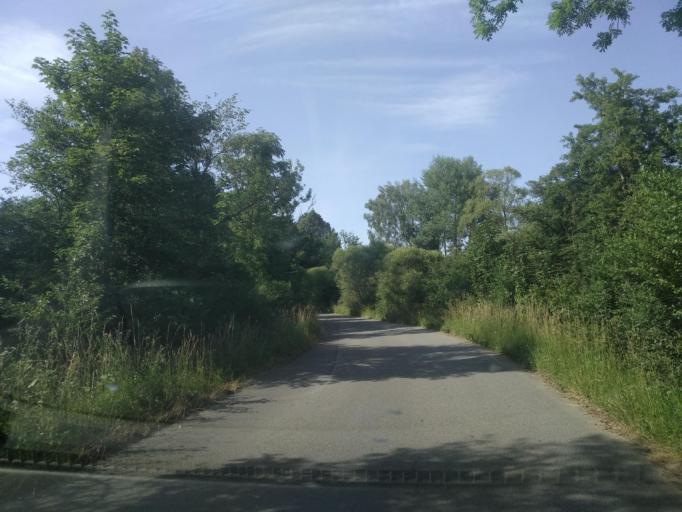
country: PL
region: Subcarpathian Voivodeship
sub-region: Powiat krosnienski
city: Jasliska
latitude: 49.4237
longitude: 21.8548
